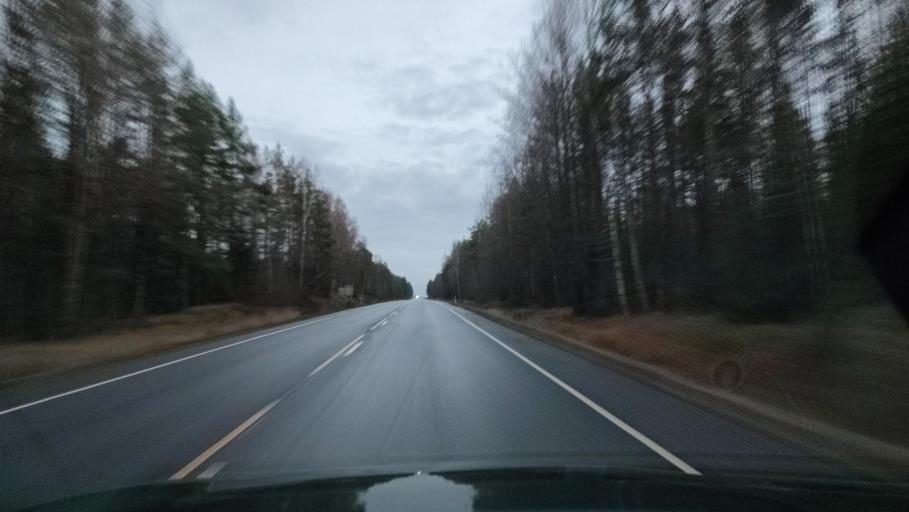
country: FI
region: Ostrobothnia
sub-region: Vaasa
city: Ristinummi
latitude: 62.9685
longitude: 21.7673
